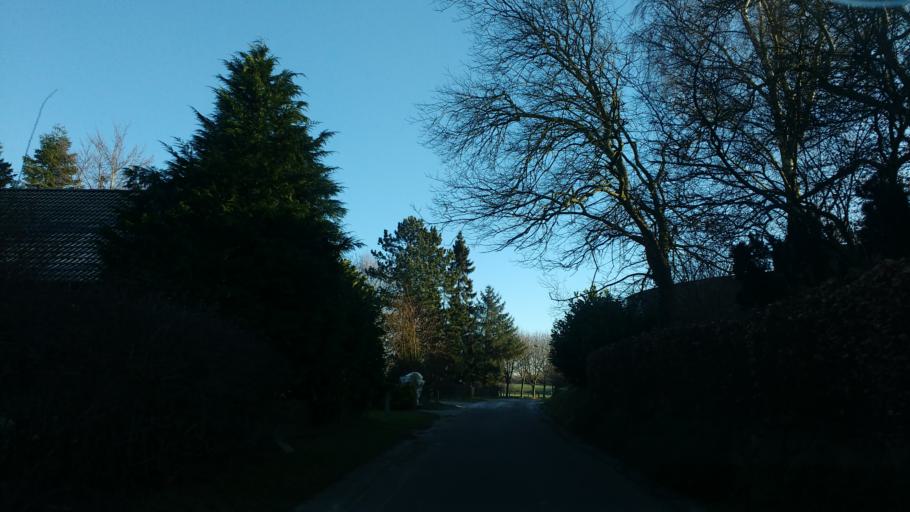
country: DE
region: Schleswig-Holstein
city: Nindorf
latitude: 54.1331
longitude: 9.7022
